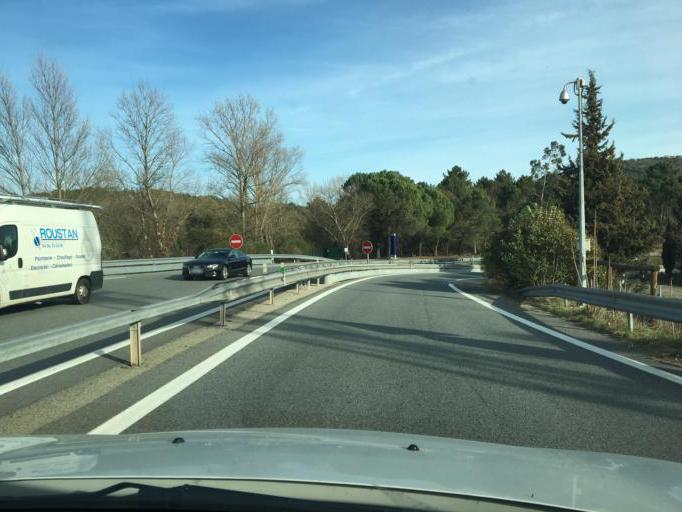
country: FR
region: Provence-Alpes-Cote d'Azur
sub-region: Departement du Var
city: Tanneron
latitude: 43.5457
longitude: 6.8113
